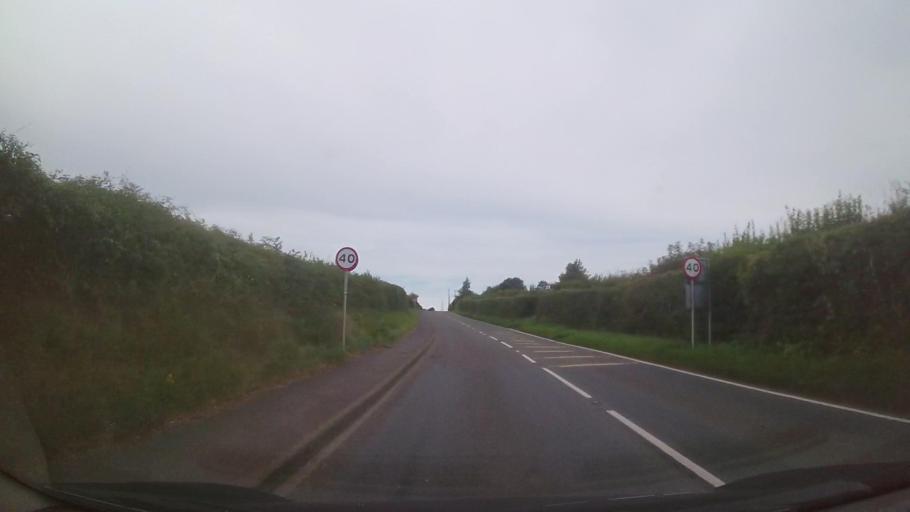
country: GB
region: Wales
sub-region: Pembrokeshire
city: Kilgetty
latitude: 51.7409
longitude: -4.7290
